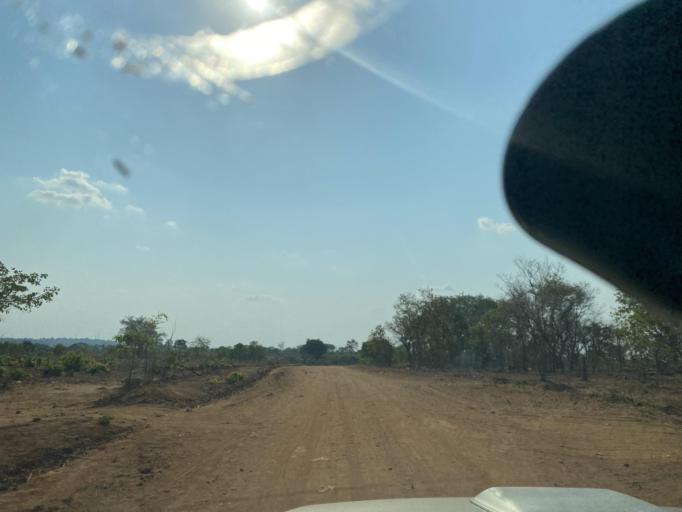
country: ZM
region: Lusaka
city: Chongwe
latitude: -15.3159
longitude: 28.7131
